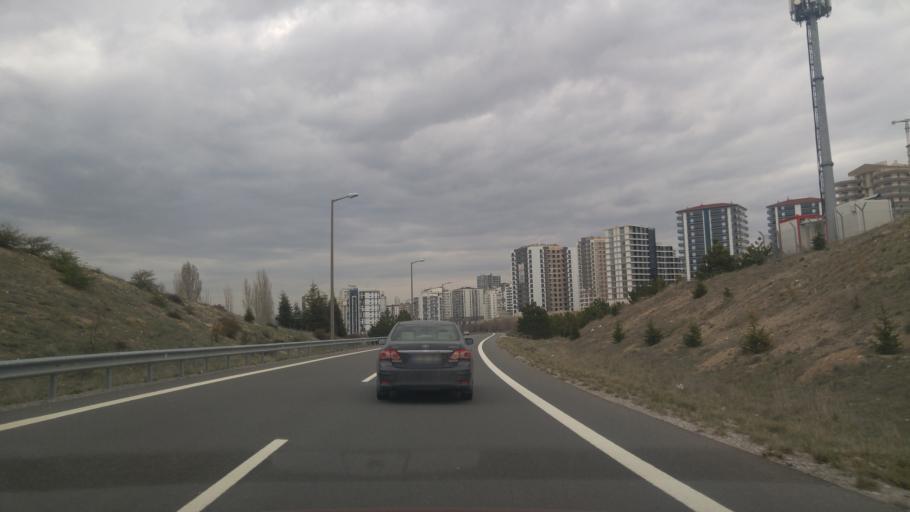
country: TR
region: Ankara
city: Etimesgut
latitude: 39.8578
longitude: 32.6276
